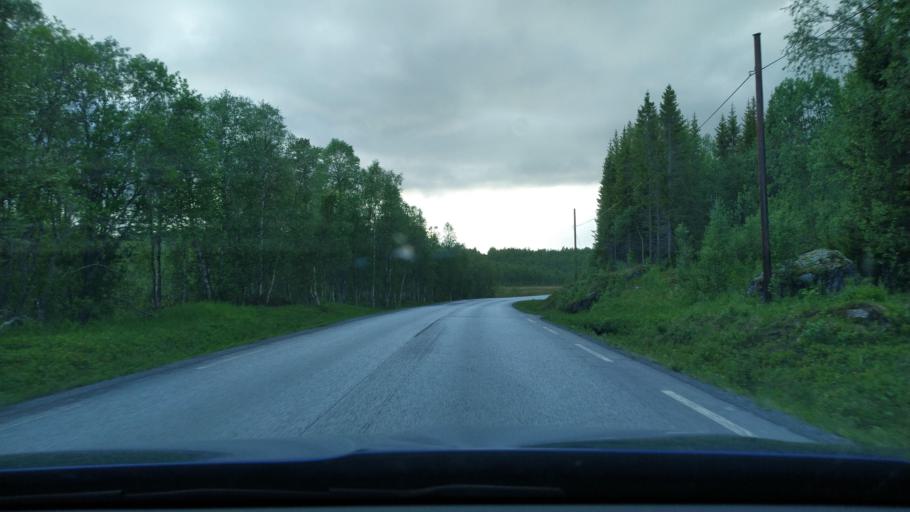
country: NO
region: Troms
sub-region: Dyroy
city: Brostadbotn
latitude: 69.0557
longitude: 17.7883
